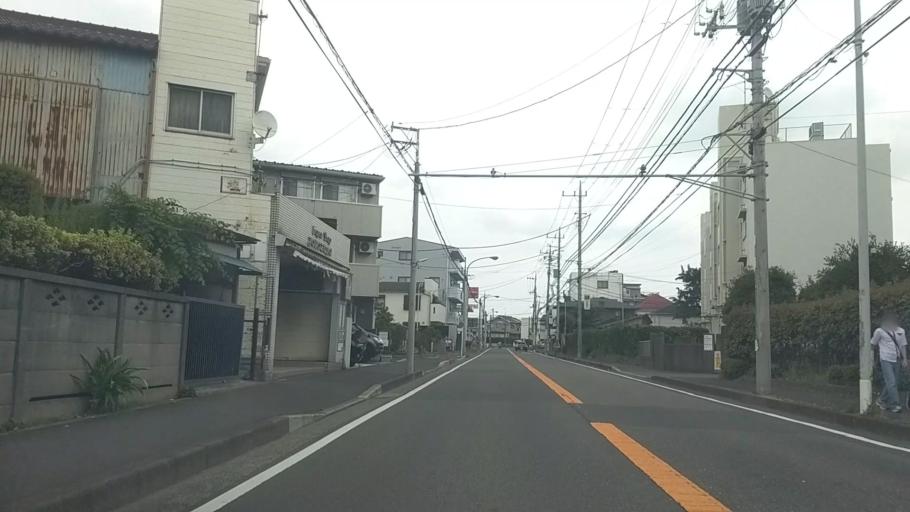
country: JP
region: Kanagawa
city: Fujisawa
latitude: 35.3423
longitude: 139.4687
